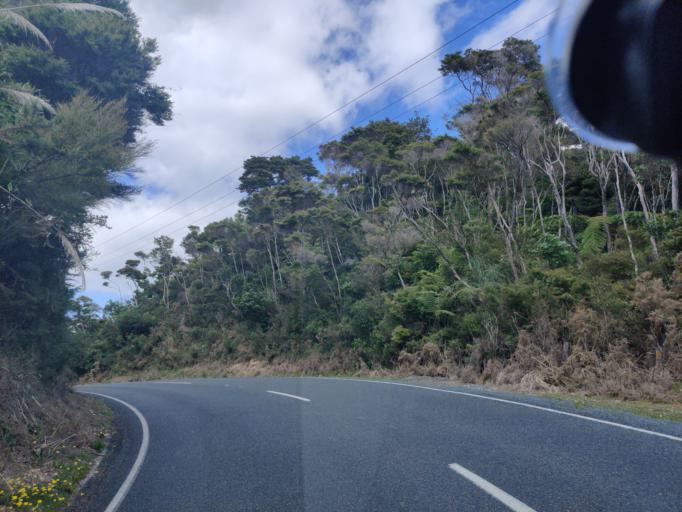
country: NZ
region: Northland
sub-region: Far North District
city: Paihia
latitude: -35.2600
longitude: 174.2199
